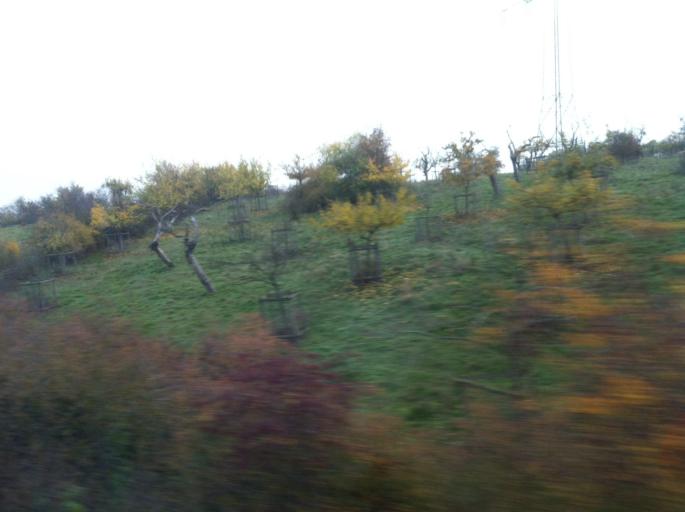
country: LU
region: Luxembourg
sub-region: Canton d'Esch-sur-Alzette
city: Bettembourg
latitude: 49.5155
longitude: 6.0888
